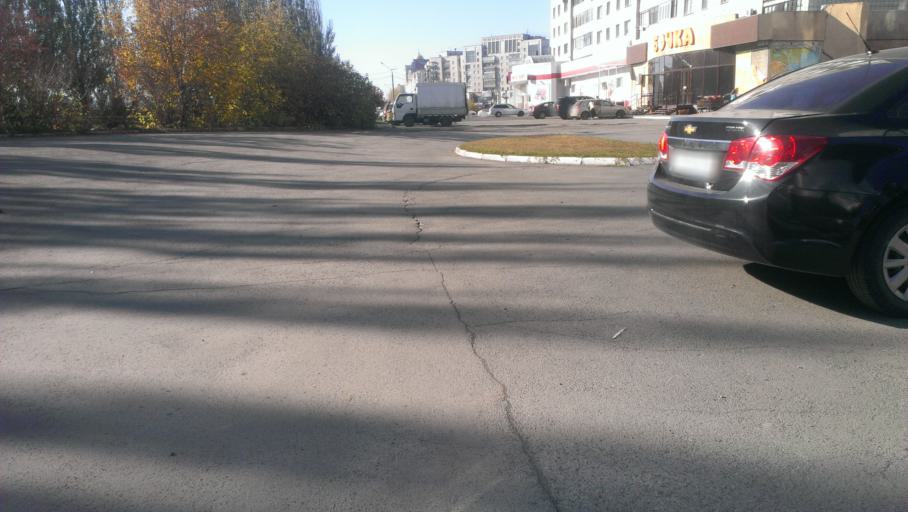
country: RU
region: Altai Krai
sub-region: Gorod Barnaulskiy
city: Barnaul
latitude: 53.3423
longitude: 83.6991
